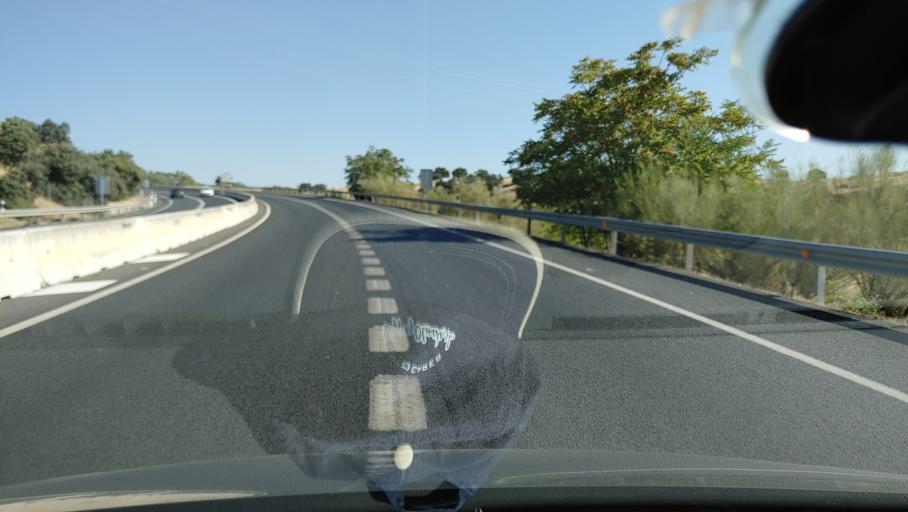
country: ES
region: Andalusia
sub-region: Province of Cordoba
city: Cordoba
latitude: 37.9096
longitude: -4.7531
